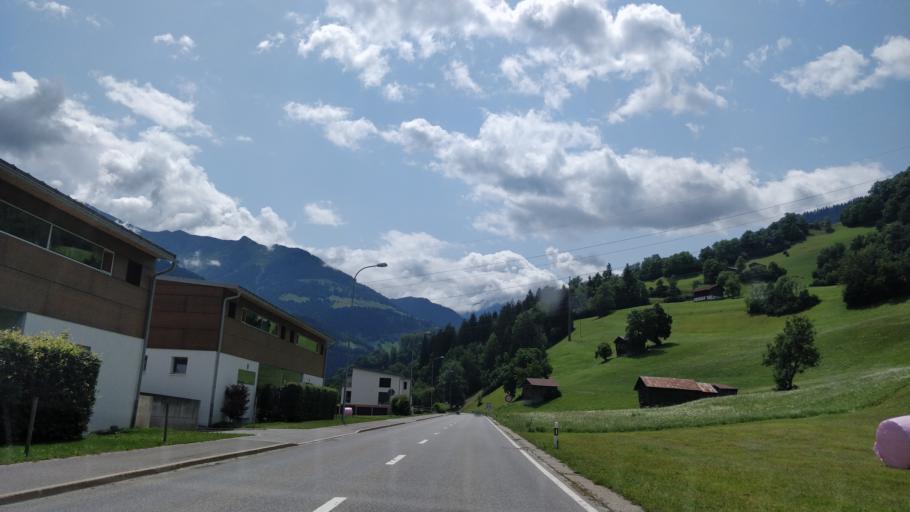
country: CH
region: Grisons
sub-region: Surselva District
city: Ilanz
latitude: 46.7689
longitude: 9.2036
